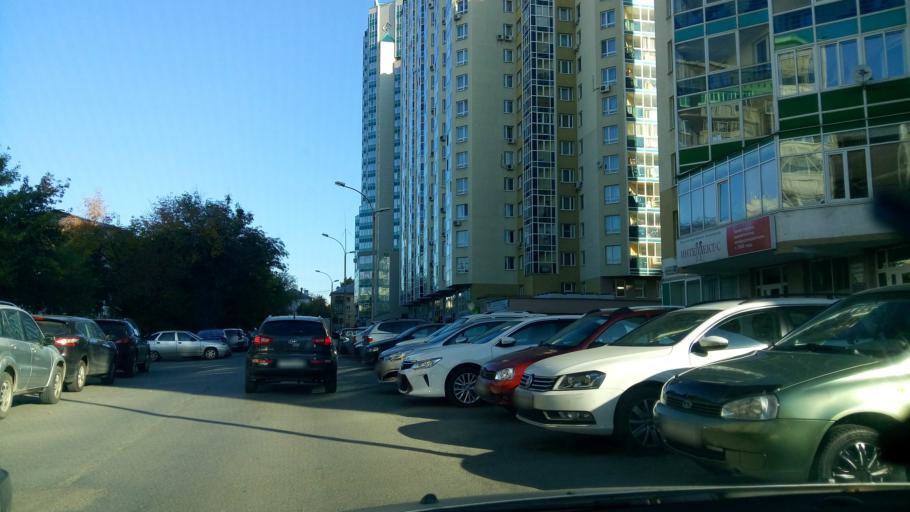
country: RU
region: Sverdlovsk
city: Yekaterinburg
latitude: 56.8471
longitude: 60.6207
